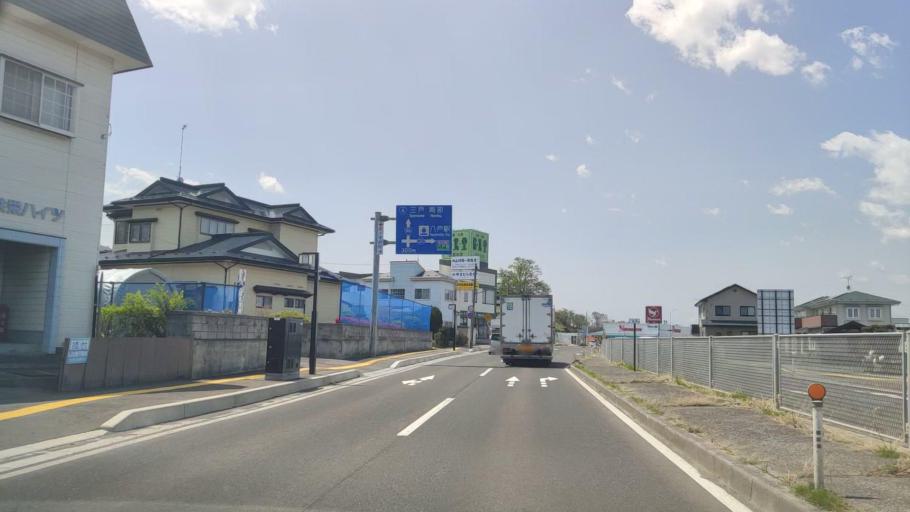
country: JP
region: Aomori
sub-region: Hachinohe Shi
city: Uchimaru
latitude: 40.5000
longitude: 141.4513
